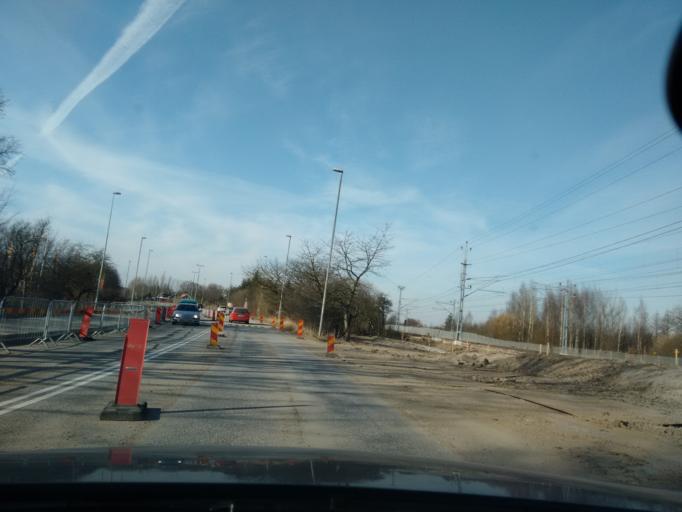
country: SE
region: Skane
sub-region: Lunds Kommun
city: Lund
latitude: 55.7234
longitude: 13.1831
